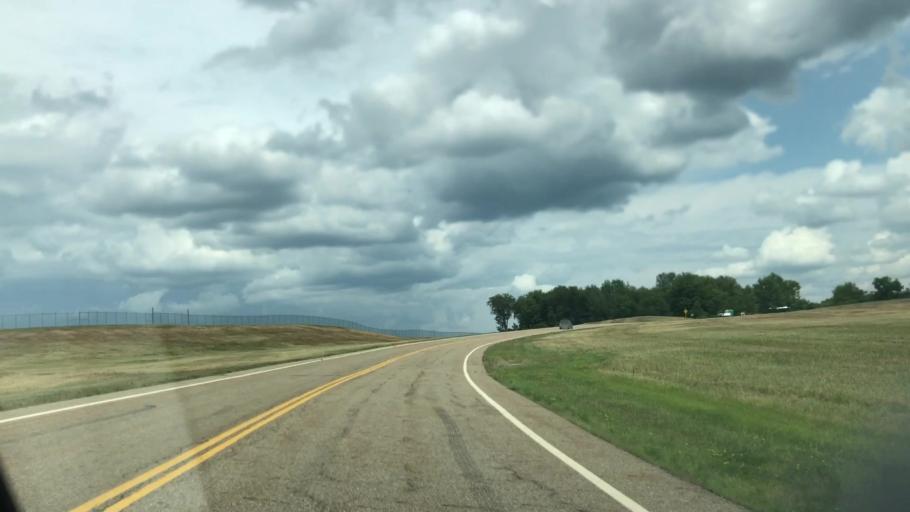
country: US
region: Ohio
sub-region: Summit County
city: Greensburg
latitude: 40.9069
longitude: -81.4504
